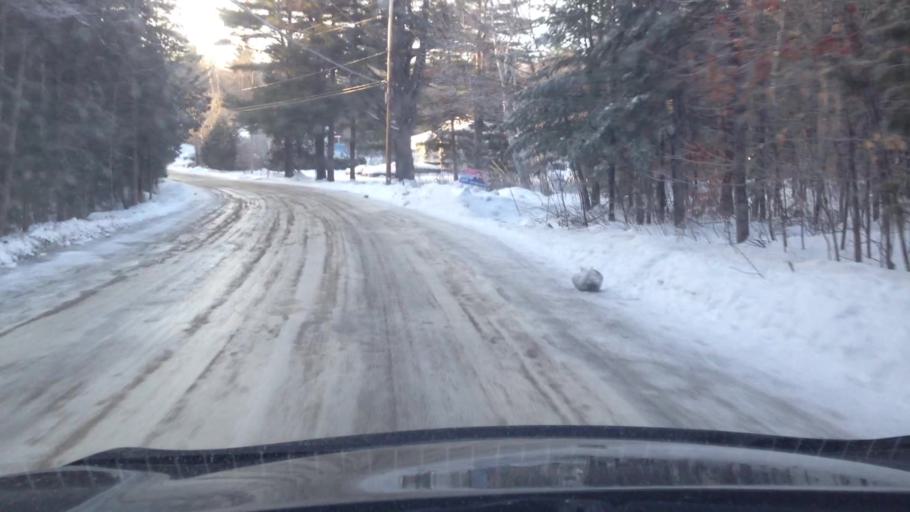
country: CA
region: Quebec
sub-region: Lanaudiere
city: Sainte-Julienne
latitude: 45.9534
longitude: -73.7577
